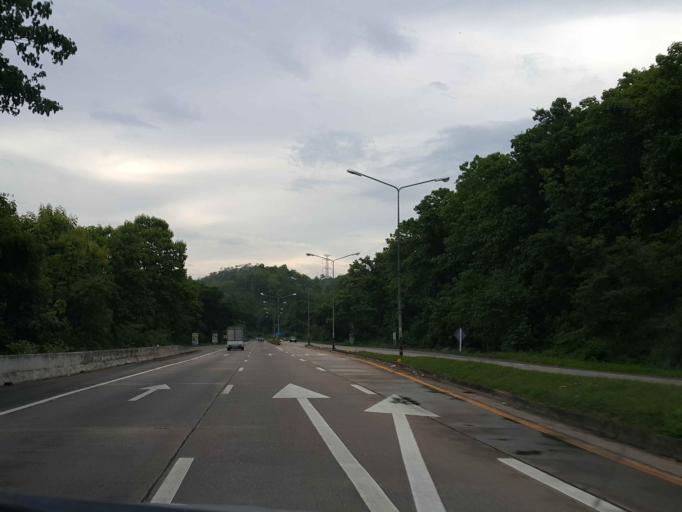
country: TH
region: Lampang
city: Hang Chat
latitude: 18.3270
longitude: 99.2645
